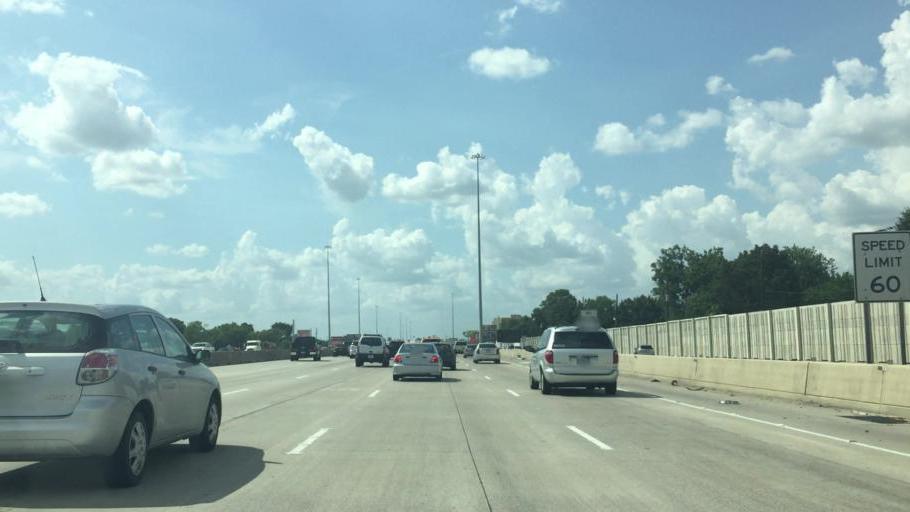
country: US
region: Texas
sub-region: Harris County
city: Spring Valley
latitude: 29.8278
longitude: -95.4783
